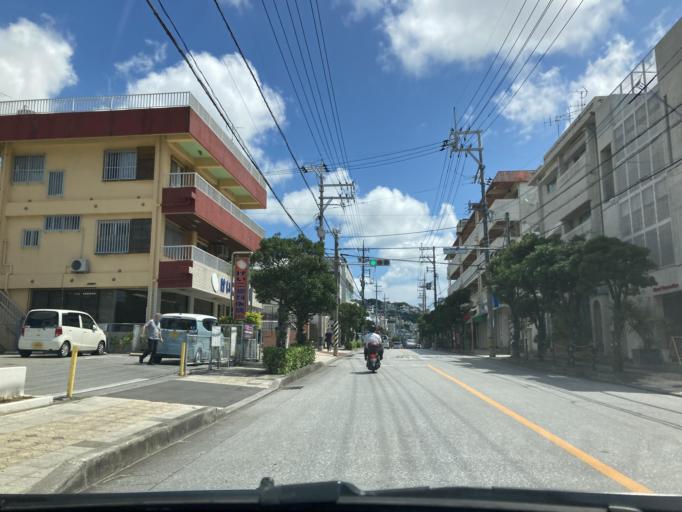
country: JP
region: Okinawa
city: Naha-shi
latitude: 26.2168
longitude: 127.7081
